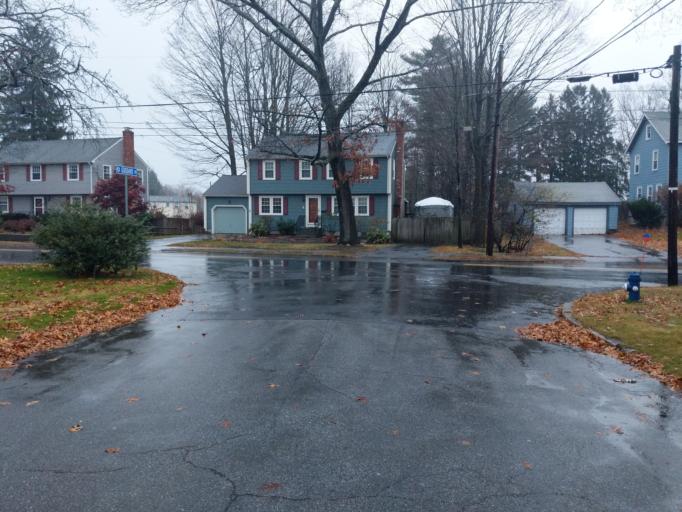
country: US
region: Massachusetts
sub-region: Middlesex County
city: Framingham Center
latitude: 42.2957
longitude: -71.4317
